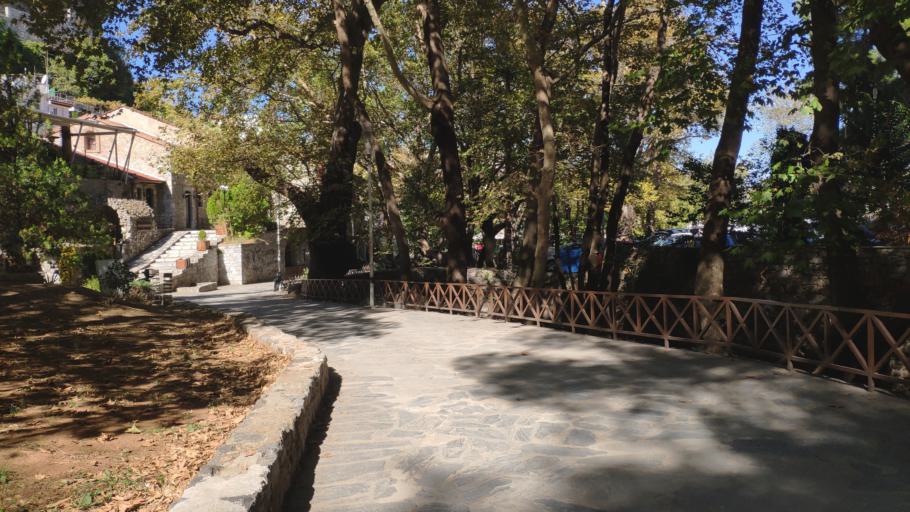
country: GR
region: Central Greece
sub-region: Nomos Voiotias
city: Livadeia
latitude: 38.4321
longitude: 22.8750
